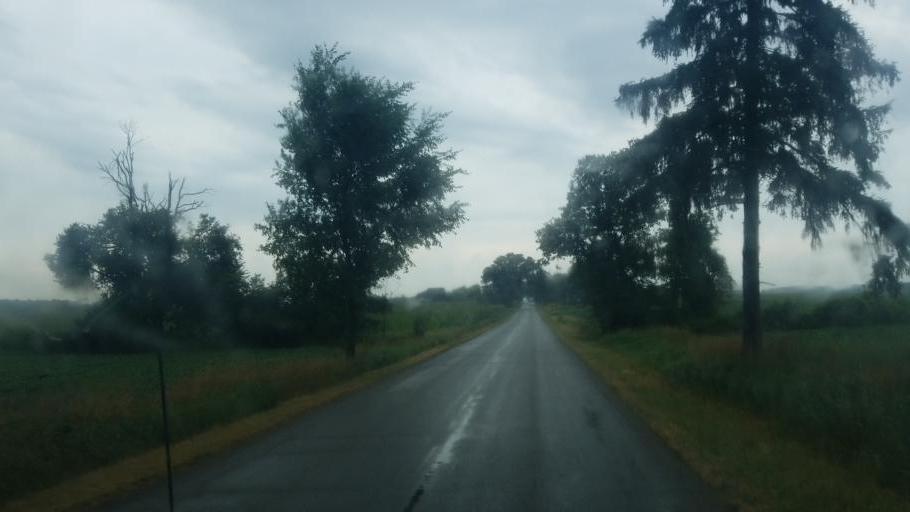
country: US
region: Indiana
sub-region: DeKalb County
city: Butler
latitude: 41.4728
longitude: -84.8667
